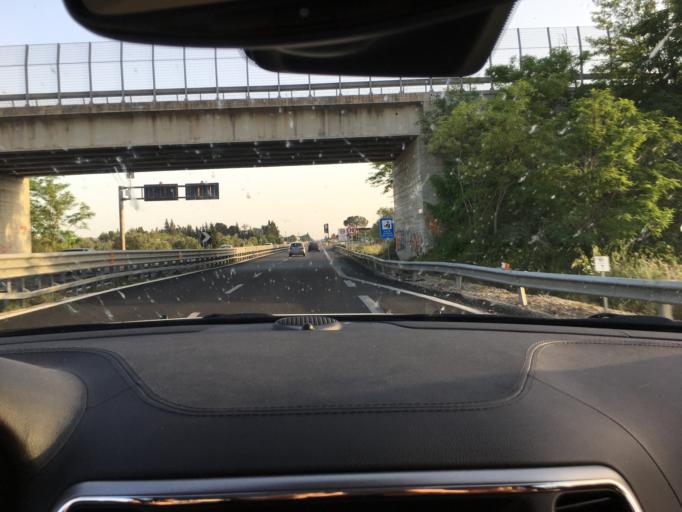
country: IT
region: Apulia
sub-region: Provincia di Lecce
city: Lequile
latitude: 40.2896
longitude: 18.1327
